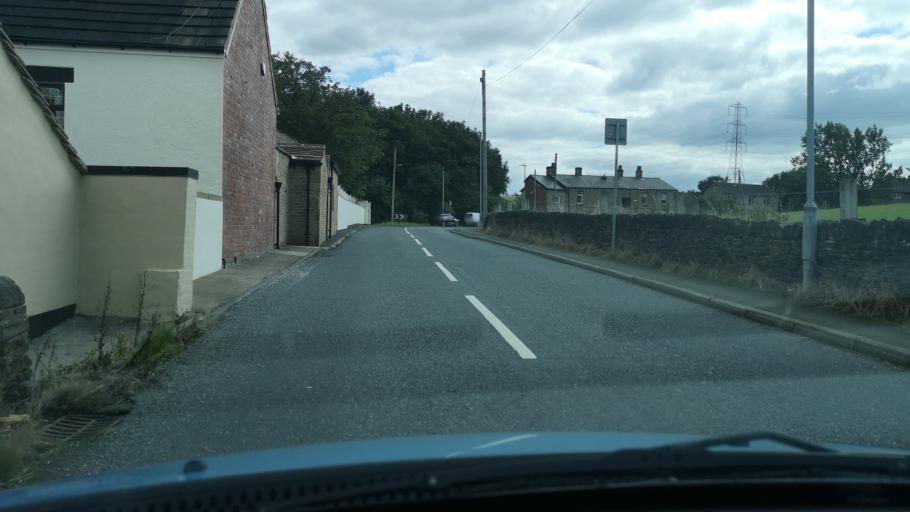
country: GB
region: England
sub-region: Kirklees
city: Mirfield
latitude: 53.6595
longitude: -1.7030
